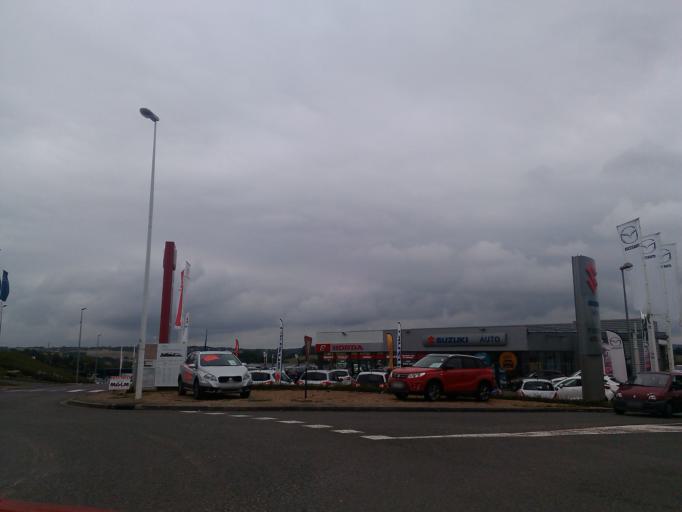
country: FR
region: Poitou-Charentes
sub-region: Departement de la Charente
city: Gond-Pontouvre
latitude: 45.6834
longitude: 0.1781
